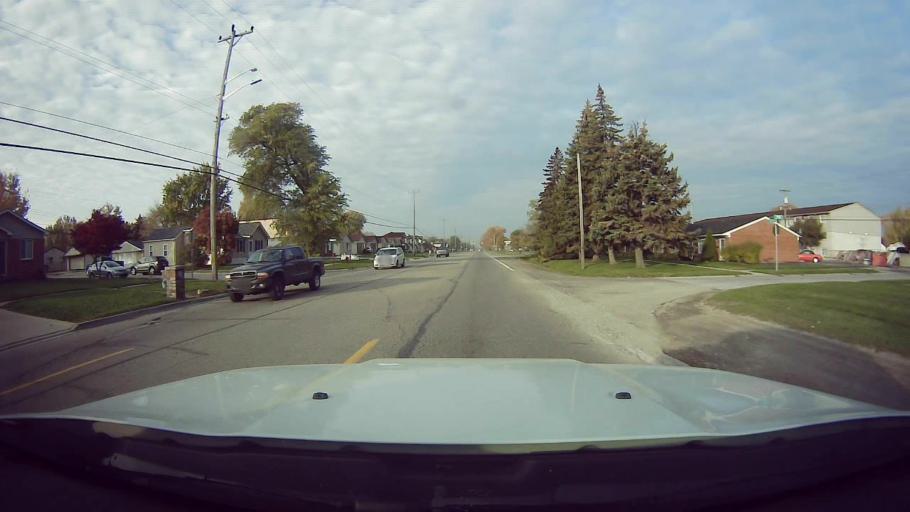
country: US
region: Michigan
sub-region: Macomb County
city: Fraser
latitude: 42.5393
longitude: -82.9159
